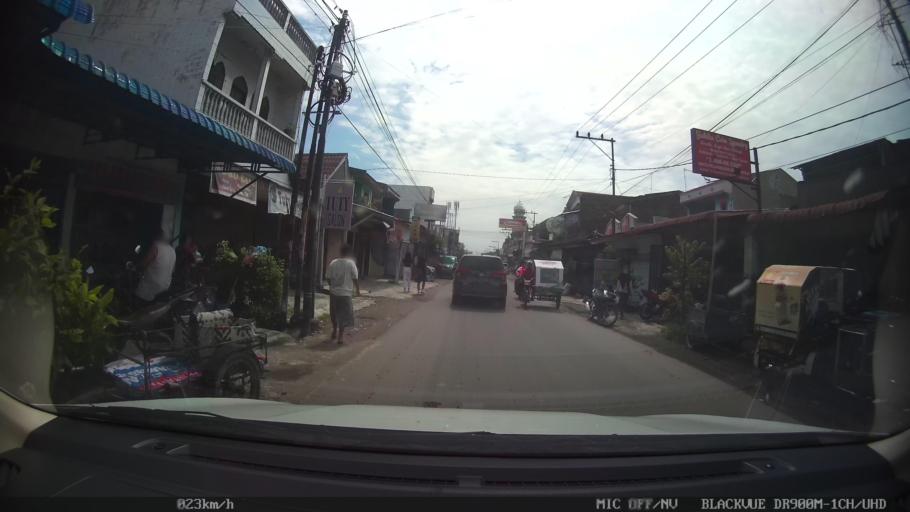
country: ID
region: North Sumatra
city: Medan
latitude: 3.5872
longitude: 98.7195
